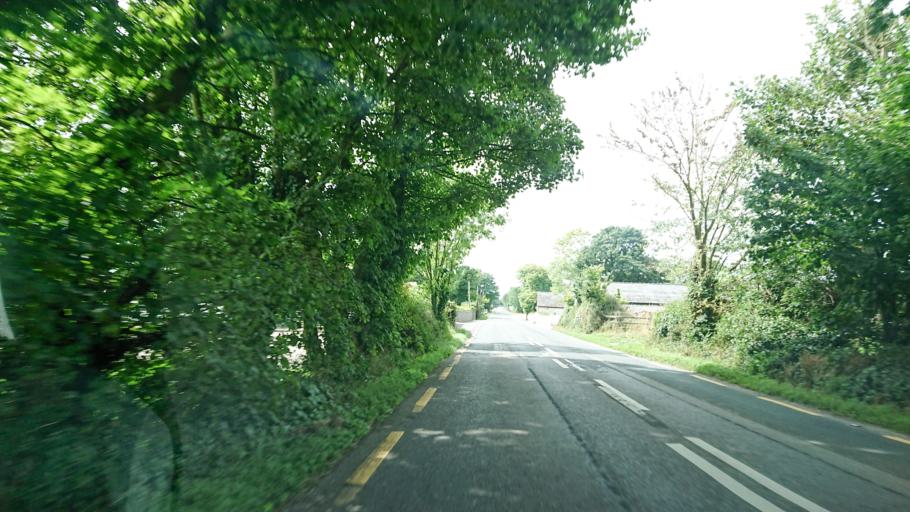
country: IE
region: Munster
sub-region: Waterford
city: Dungarvan
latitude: 52.1219
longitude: -7.7533
